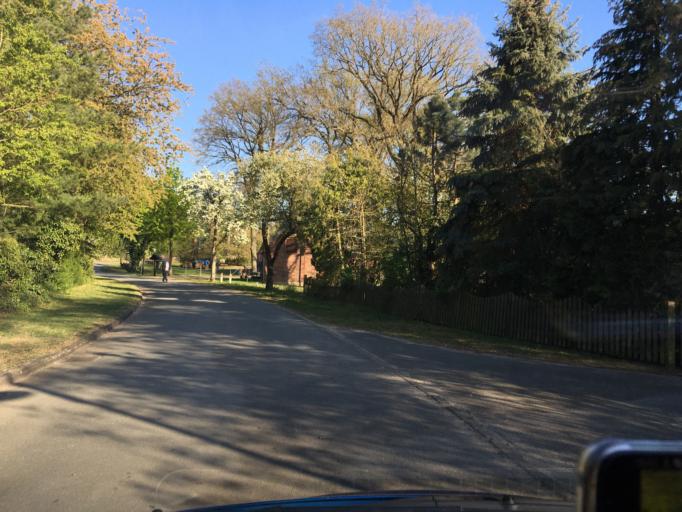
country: DE
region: Lower Saxony
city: Altenmedingen
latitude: 53.1701
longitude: 10.6144
